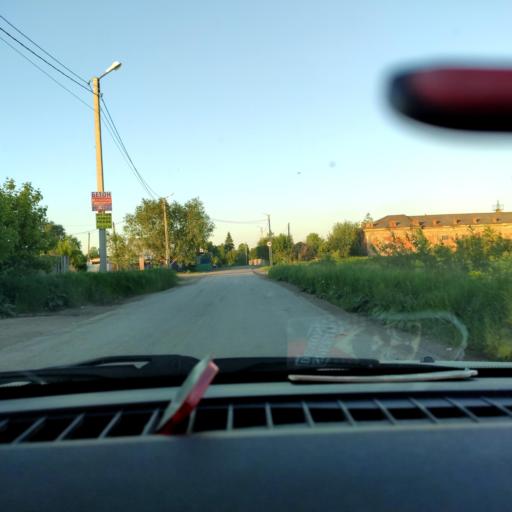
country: RU
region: Perm
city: Kondratovo
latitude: 57.9334
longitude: 56.1694
